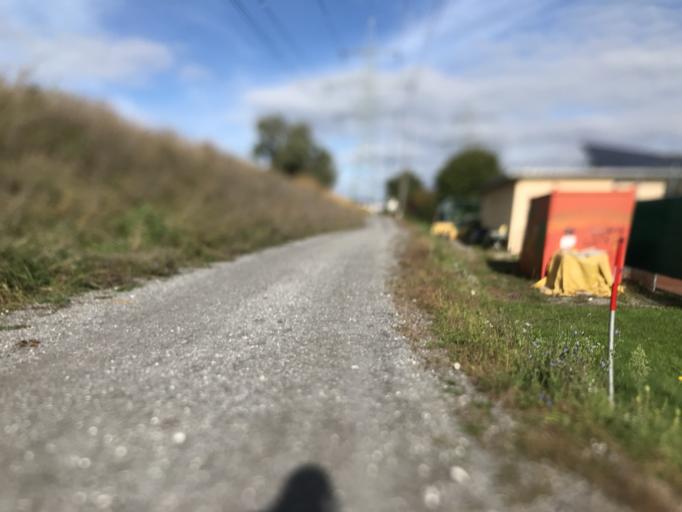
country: AT
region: Vorarlberg
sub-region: Politischer Bezirk Feldkirch
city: Mader
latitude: 47.3543
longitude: 9.6112
